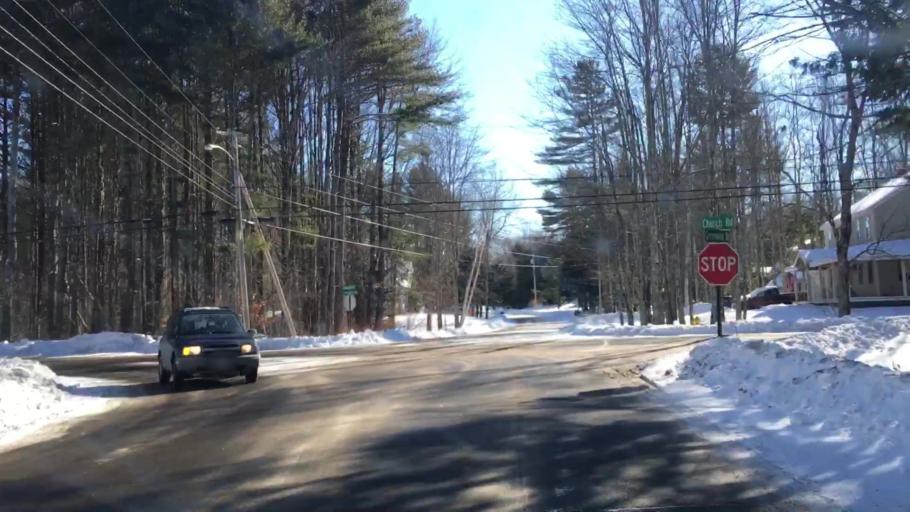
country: US
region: Maine
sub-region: Sagadahoc County
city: Topsham
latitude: 43.9029
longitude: -69.9979
